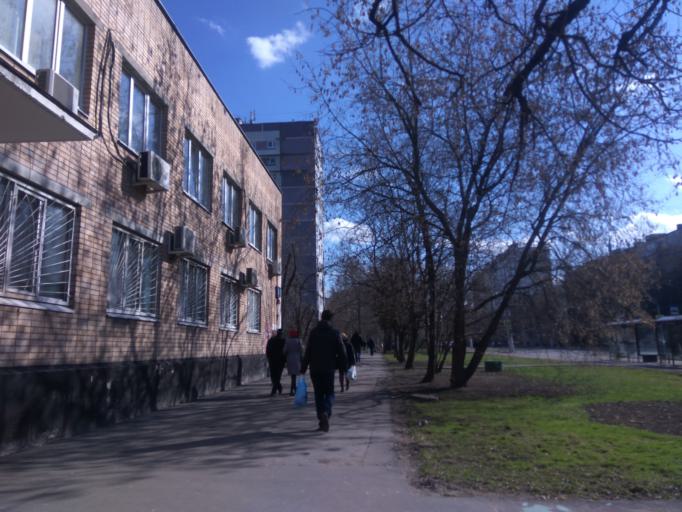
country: RU
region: Moscow
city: Ivanovskoye
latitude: 55.7622
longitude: 37.8328
